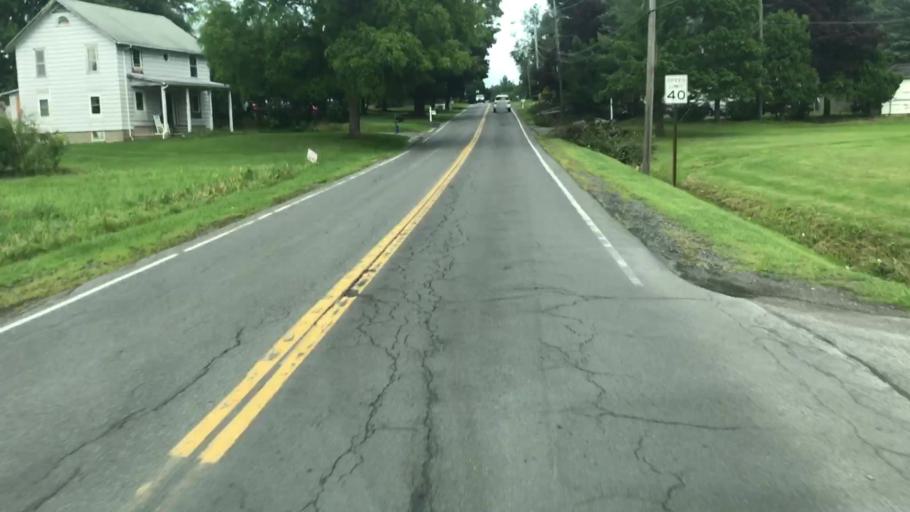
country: US
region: New York
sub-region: Cayuga County
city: Auburn
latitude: 42.9443
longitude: -76.5378
